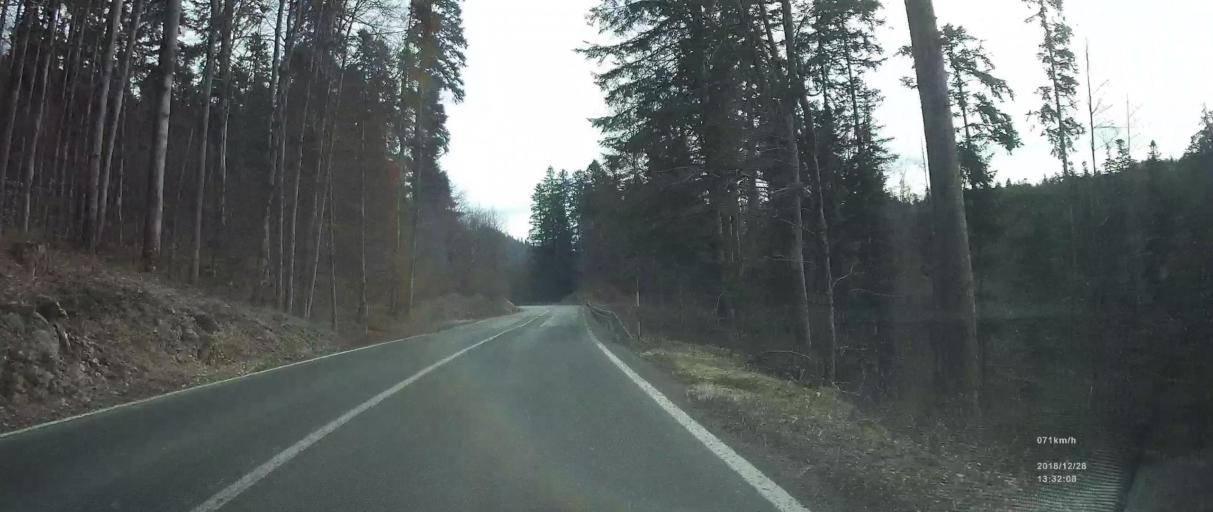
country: HR
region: Primorsko-Goranska
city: Hreljin
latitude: 45.3485
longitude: 14.6606
